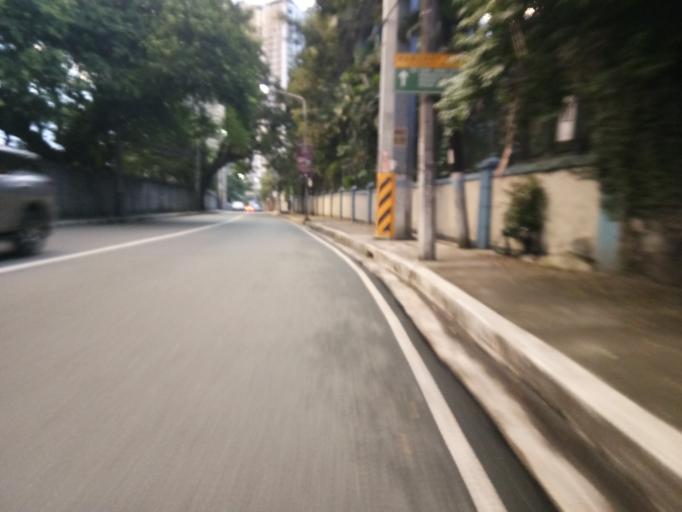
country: PH
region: Metro Manila
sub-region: San Juan
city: San Juan
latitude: 14.6162
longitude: 121.0423
